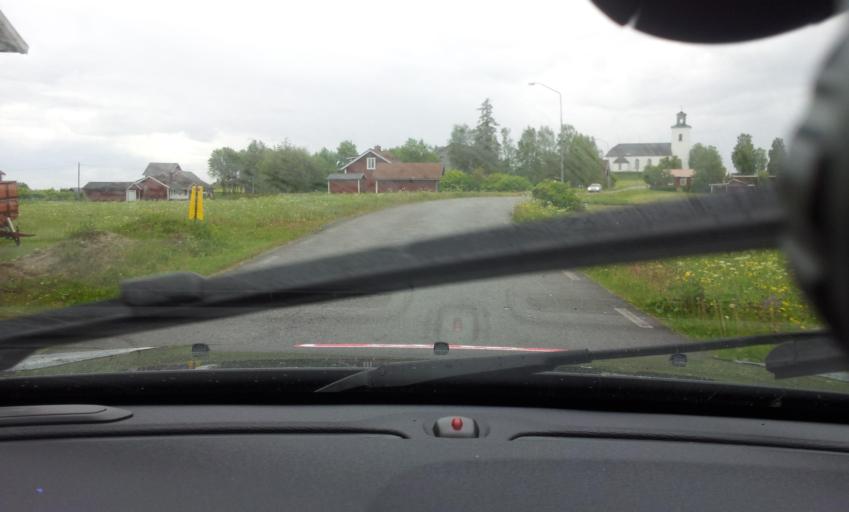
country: SE
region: Jaemtland
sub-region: Bergs Kommun
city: Hoverberg
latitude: 62.9772
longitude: 14.5767
